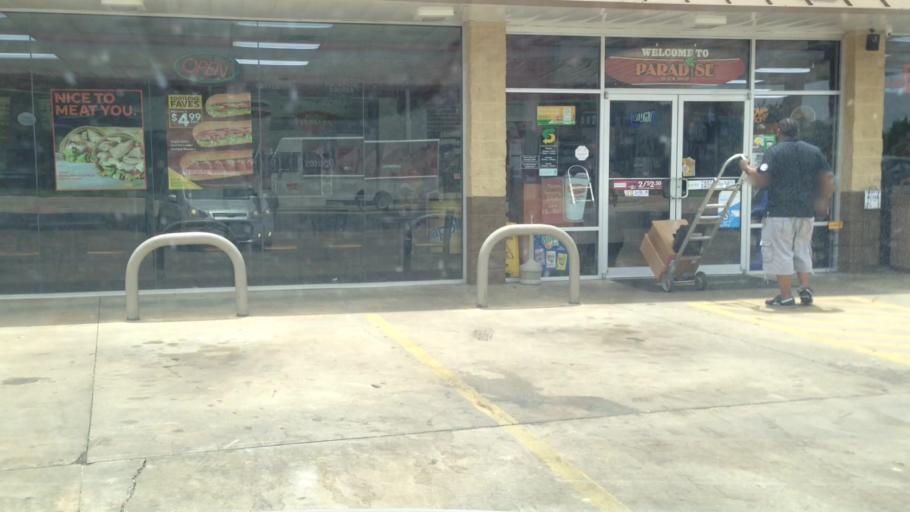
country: US
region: Texas
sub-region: Bowie County
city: Wake Village
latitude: 33.4186
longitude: -94.0941
